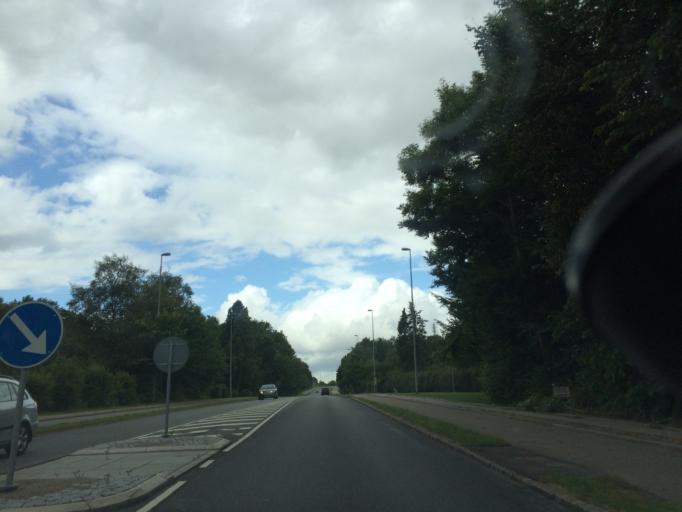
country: DK
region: Central Jutland
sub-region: Arhus Kommune
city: Stavtrup
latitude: 56.1527
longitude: 10.0837
